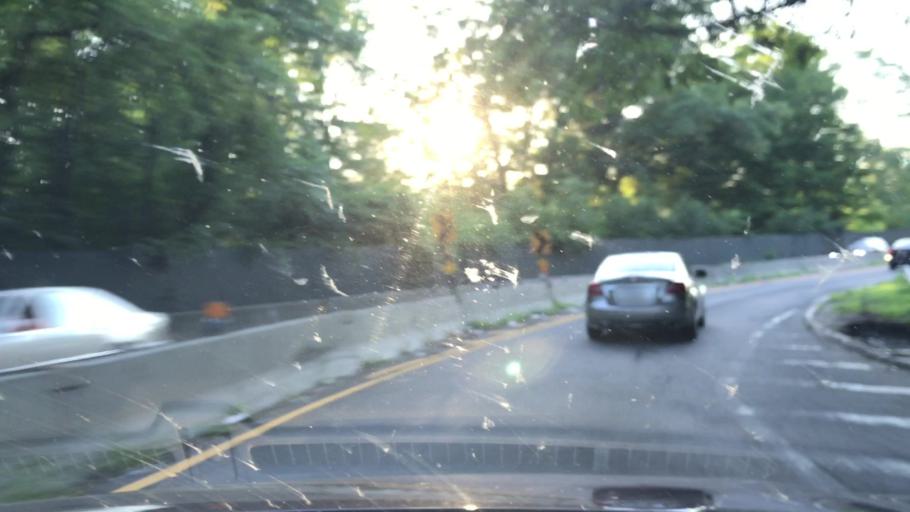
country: US
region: New York
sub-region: Bronx
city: The Bronx
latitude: 40.8670
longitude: -73.8748
